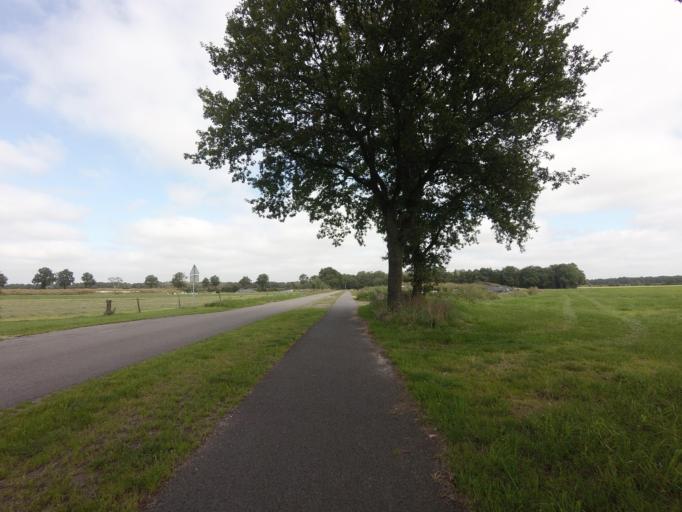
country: NL
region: Drenthe
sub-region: Gemeente Westerveld
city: Havelte
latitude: 52.8446
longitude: 6.2372
